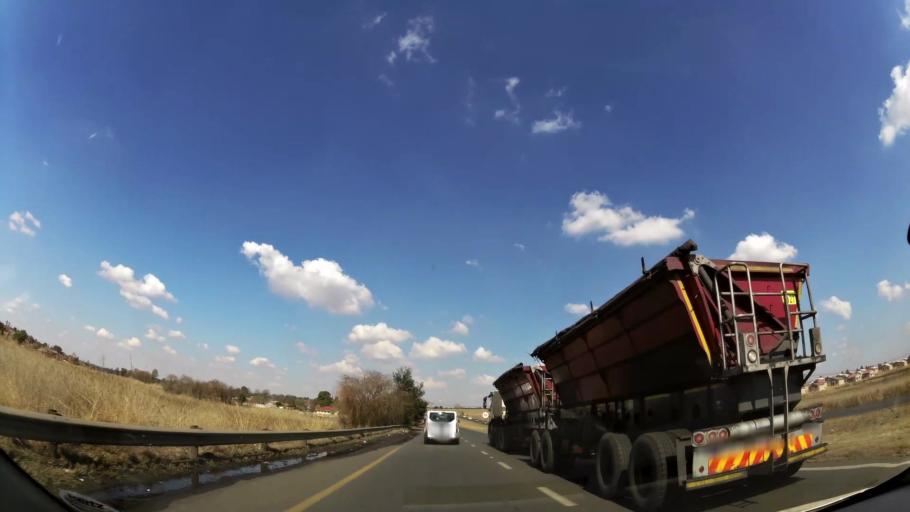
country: ZA
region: Mpumalanga
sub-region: Nkangala District Municipality
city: Witbank
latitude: -25.9309
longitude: 29.2366
